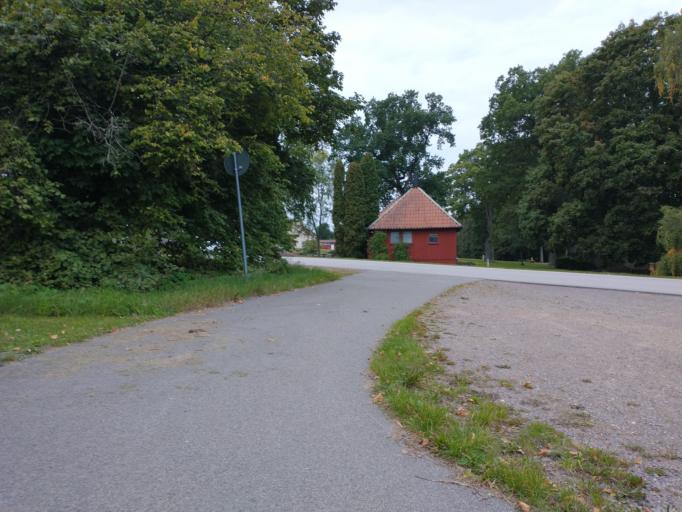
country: SE
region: Kalmar
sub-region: Kalmar Kommun
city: Lindsdal
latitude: 56.7818
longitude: 16.2884
